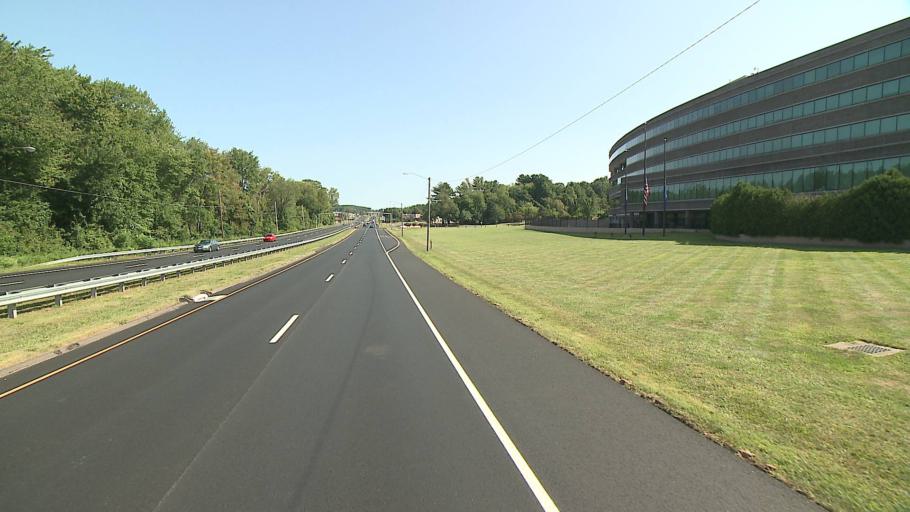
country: US
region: Connecticut
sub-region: Hartford County
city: Newington
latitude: 41.6732
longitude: -72.7158
